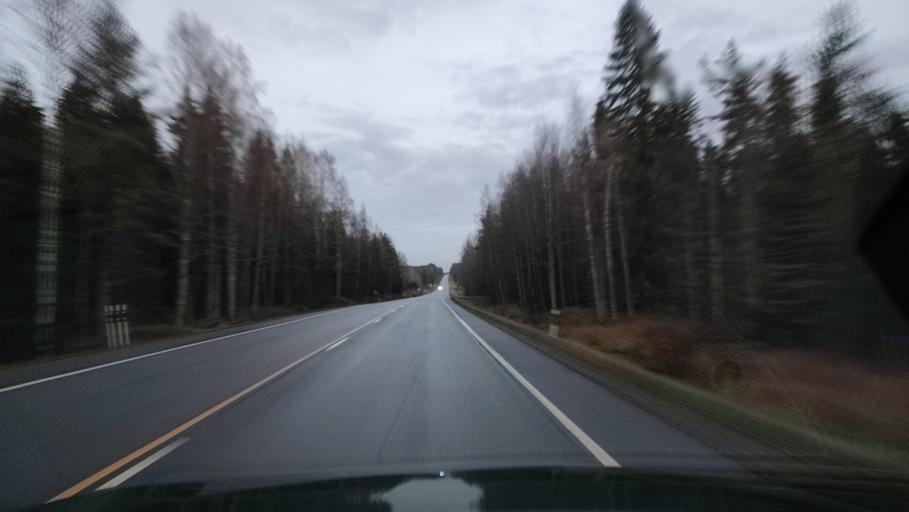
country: FI
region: Ostrobothnia
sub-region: Vaasa
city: Ristinummi
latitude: 62.9762
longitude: 21.7690
